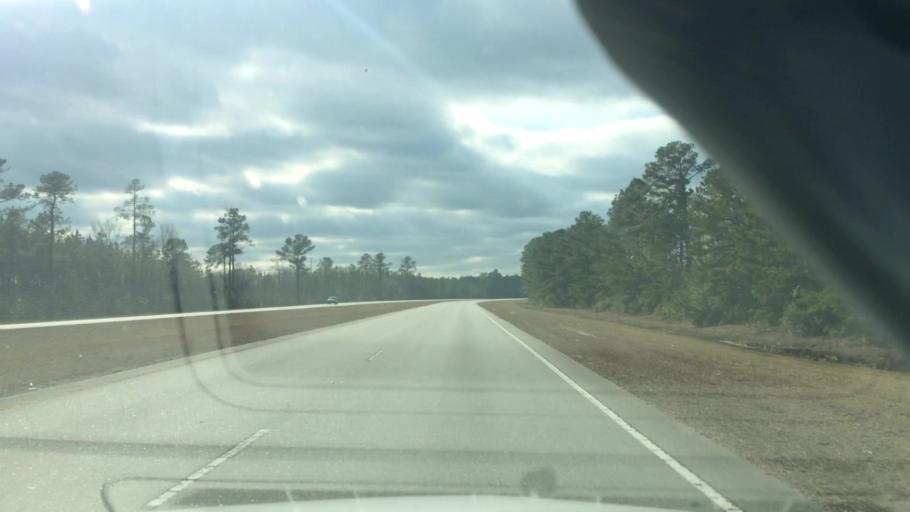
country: US
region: North Carolina
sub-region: Brunswick County
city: Bolivia
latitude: 34.0522
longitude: -78.2170
